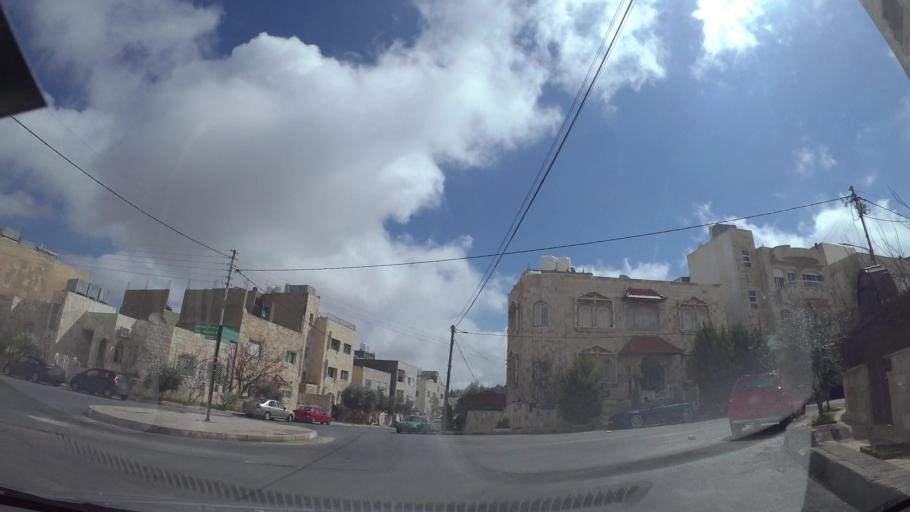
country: JO
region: Amman
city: Al Jubayhah
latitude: 32.0626
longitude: 35.8743
